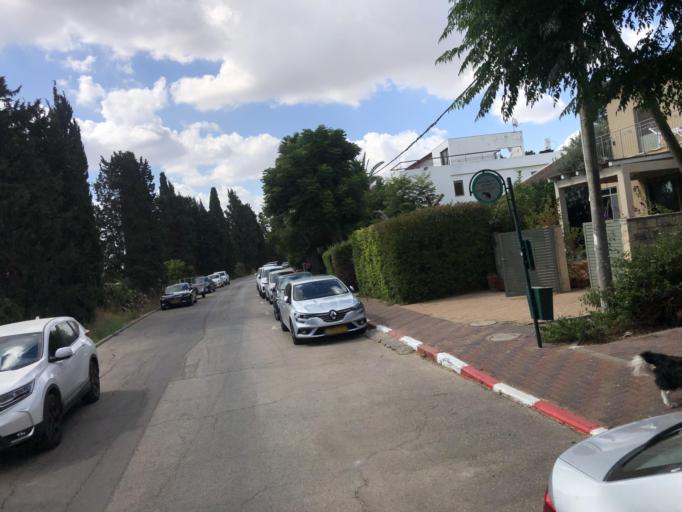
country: IL
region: Central District
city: Yehud
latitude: 32.0392
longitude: 34.8979
